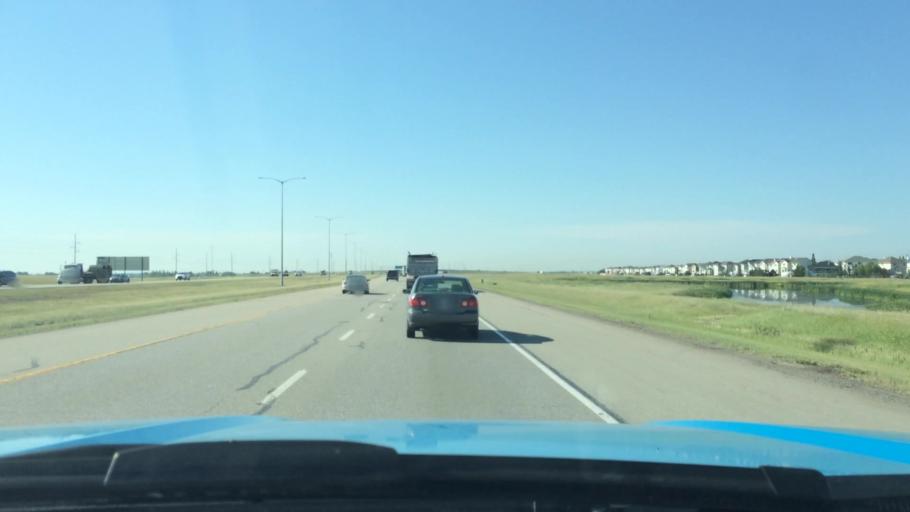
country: CA
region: Alberta
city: Chestermere
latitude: 51.1128
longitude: -113.9211
